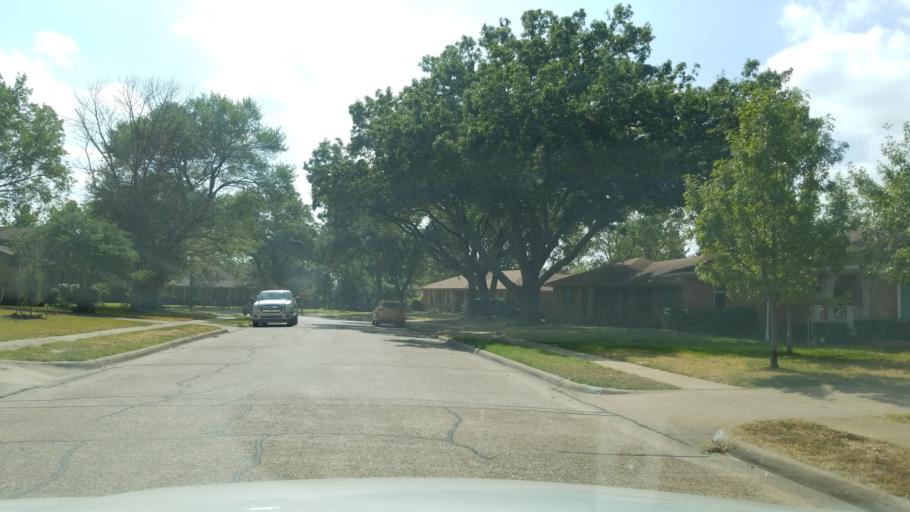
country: US
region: Texas
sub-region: Dallas County
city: Garland
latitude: 32.8938
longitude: -96.6625
